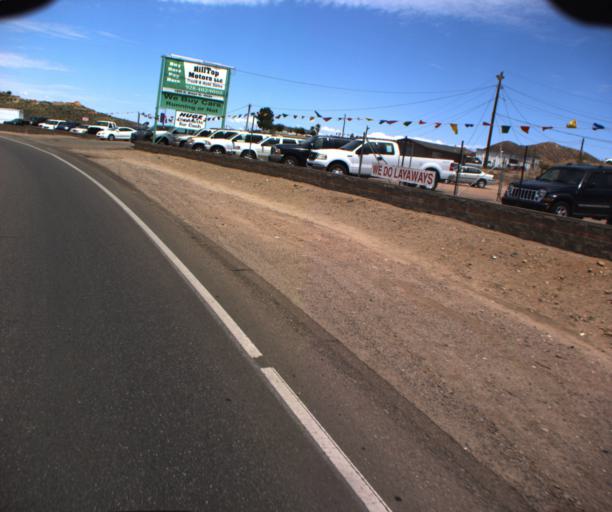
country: US
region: Arizona
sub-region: Gila County
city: Central Heights-Midland City
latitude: 33.4193
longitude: -110.8062
